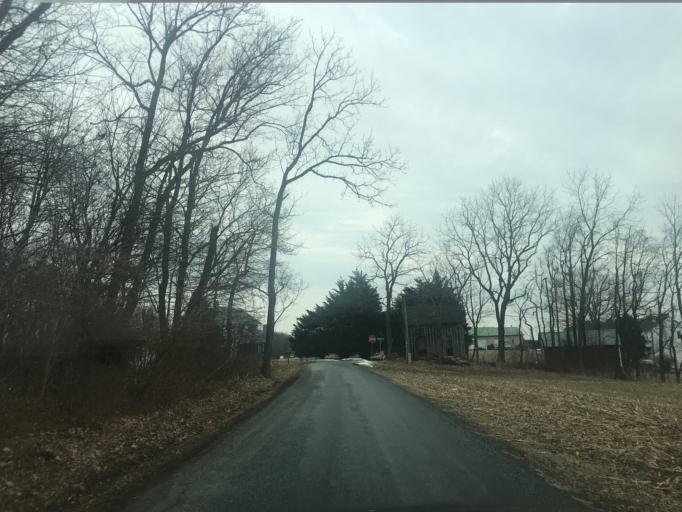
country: US
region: Maryland
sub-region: Harford County
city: Jarrettsville
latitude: 39.6973
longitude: -76.5099
